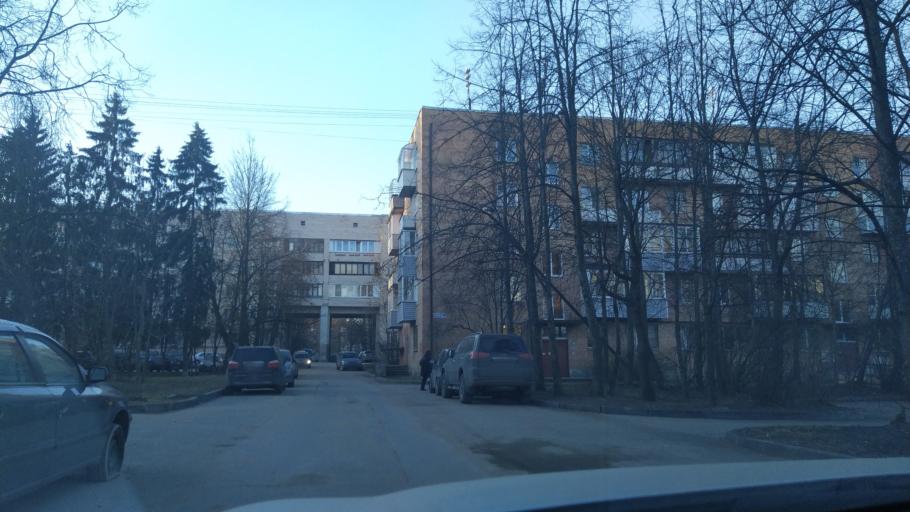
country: RU
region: St.-Petersburg
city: Pushkin
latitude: 59.7278
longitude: 30.4062
